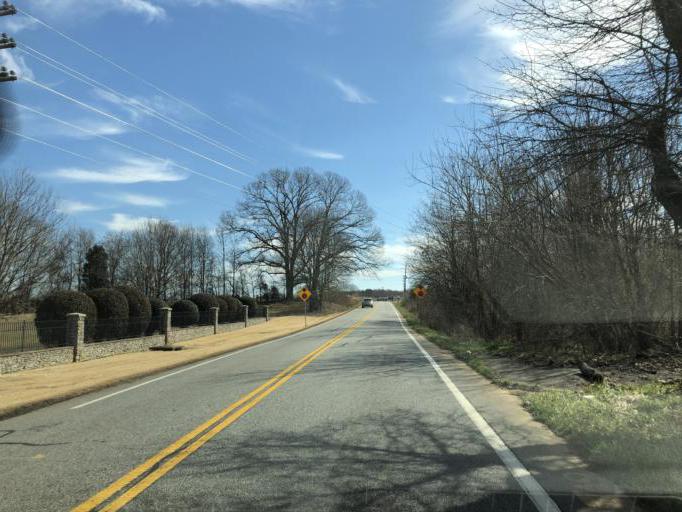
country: US
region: South Carolina
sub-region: Spartanburg County
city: Boiling Springs
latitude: 35.0517
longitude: -81.9289
